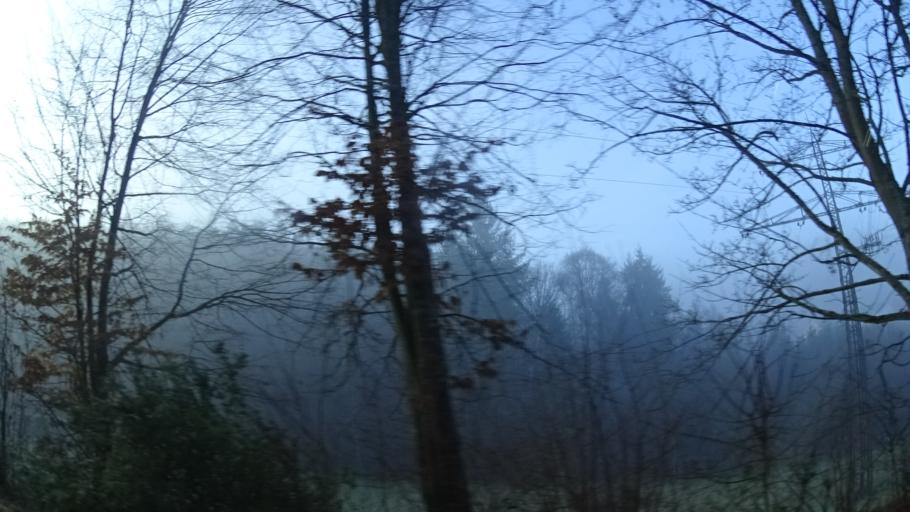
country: DE
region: Bavaria
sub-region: Regierungsbezirk Unterfranken
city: Neunkirchen
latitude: 49.7294
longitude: 9.4135
